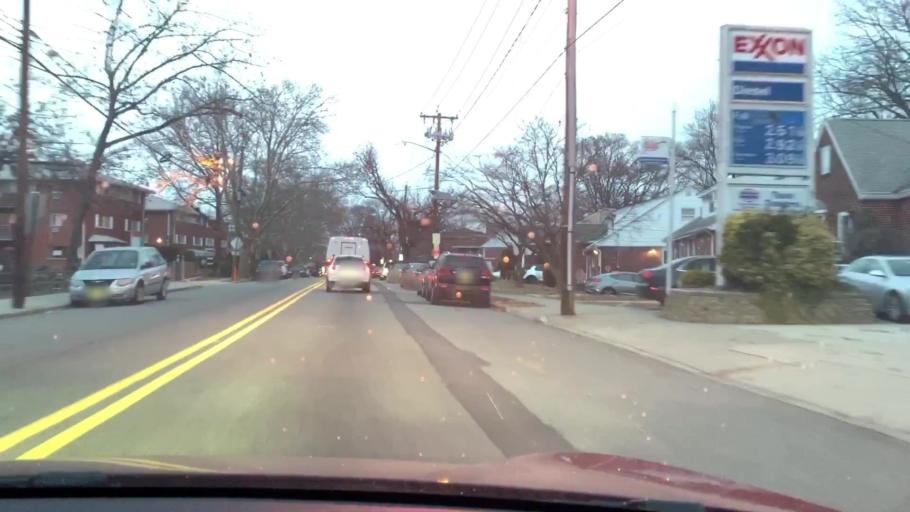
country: US
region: New Jersey
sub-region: Bergen County
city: Fort Lee
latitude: 40.8419
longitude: -73.9801
